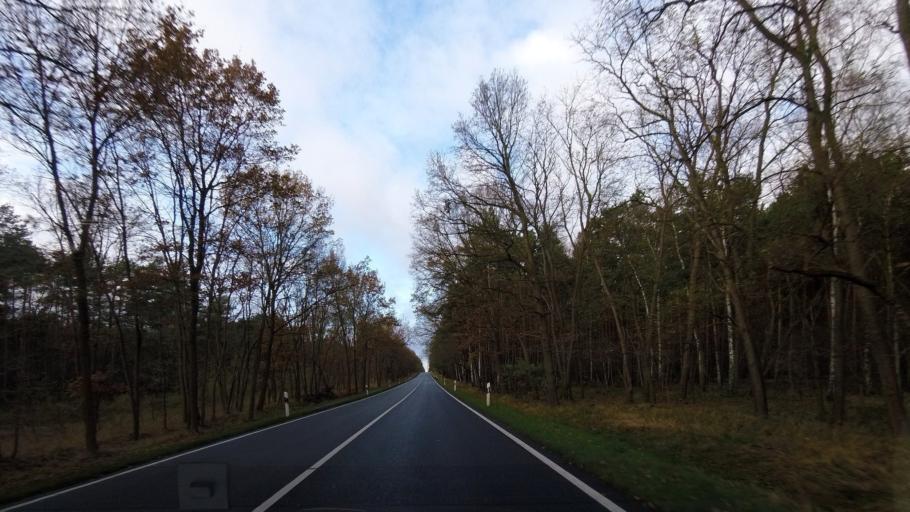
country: DE
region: Brandenburg
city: Treuenbrietzen
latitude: 52.0442
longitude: 12.9198
